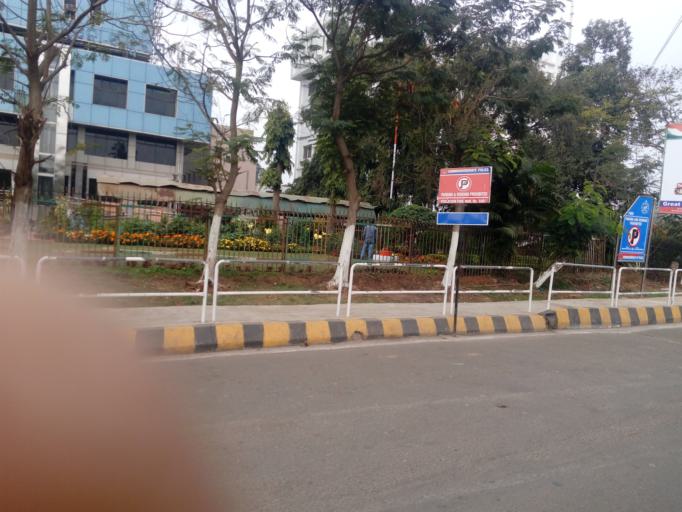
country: IN
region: Odisha
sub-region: Khordha
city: Bhubaneshwar
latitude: 20.2888
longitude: 85.8428
